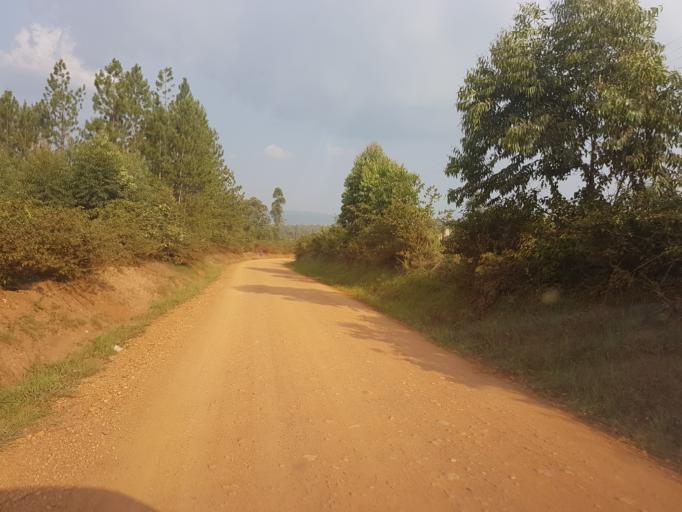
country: UG
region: Western Region
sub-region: Rukungiri District
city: Rukungiri
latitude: -0.6577
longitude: 29.8621
